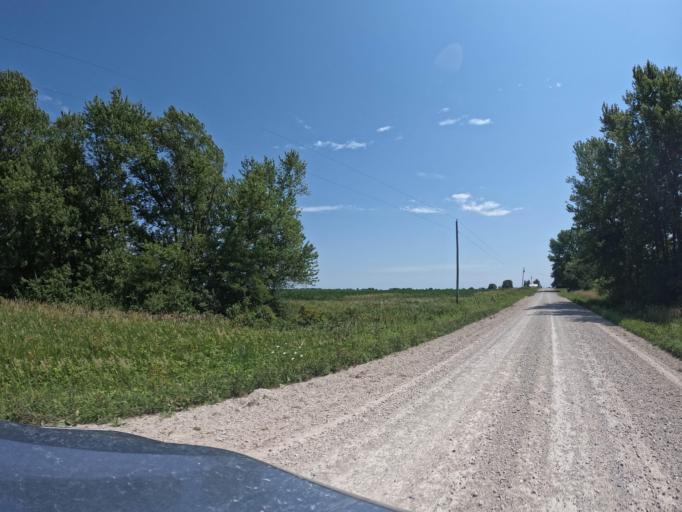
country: US
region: Iowa
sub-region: Henry County
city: Mount Pleasant
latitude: 40.9057
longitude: -91.6316
